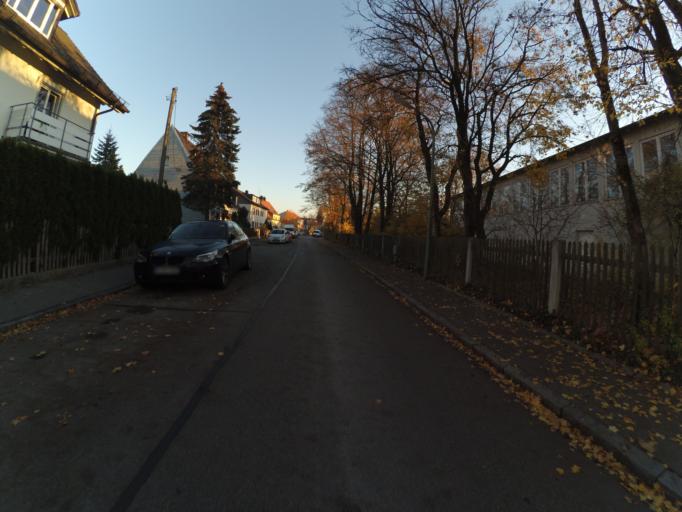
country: DE
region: Bavaria
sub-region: Upper Bavaria
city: Oberschleissheim
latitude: 48.1969
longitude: 11.5504
